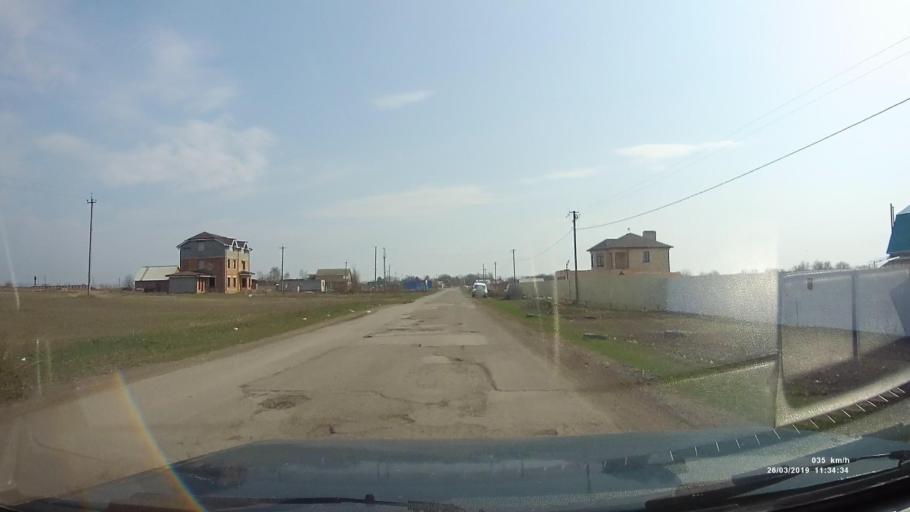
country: RU
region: Rostov
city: Novobessergenovka
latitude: 47.1470
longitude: 38.6312
